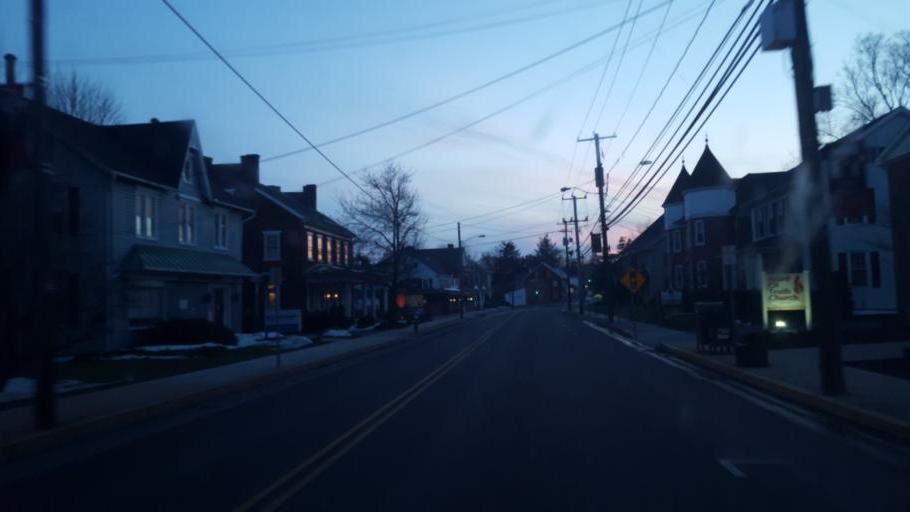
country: US
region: Pennsylvania
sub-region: Lancaster County
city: New Holland
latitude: 40.1021
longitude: -76.0903
